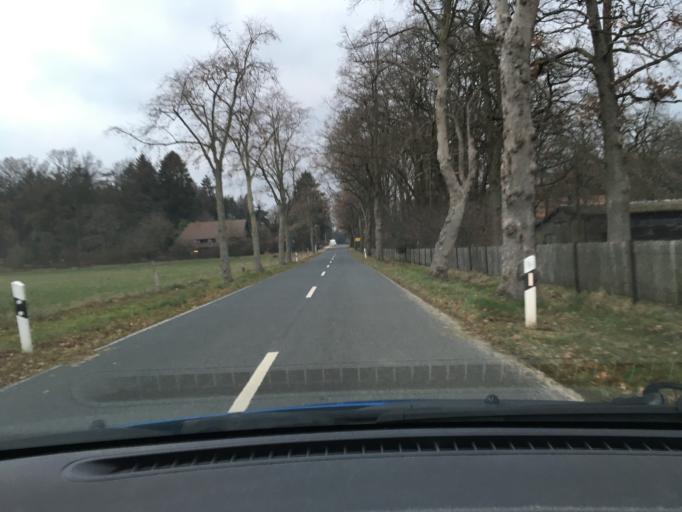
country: DE
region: Lower Saxony
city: Walsrode
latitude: 52.8313
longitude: 9.5761
